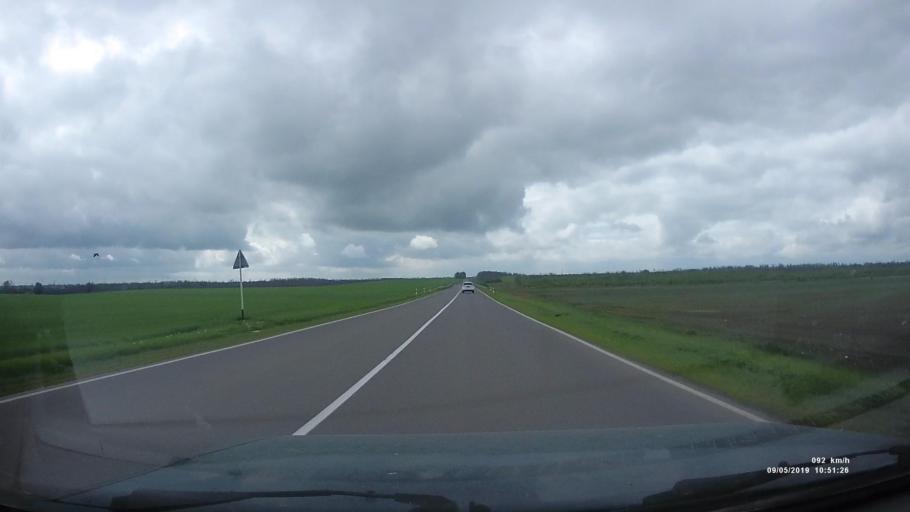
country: RU
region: Rostov
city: Peshkovo
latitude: 46.9157
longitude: 39.3550
